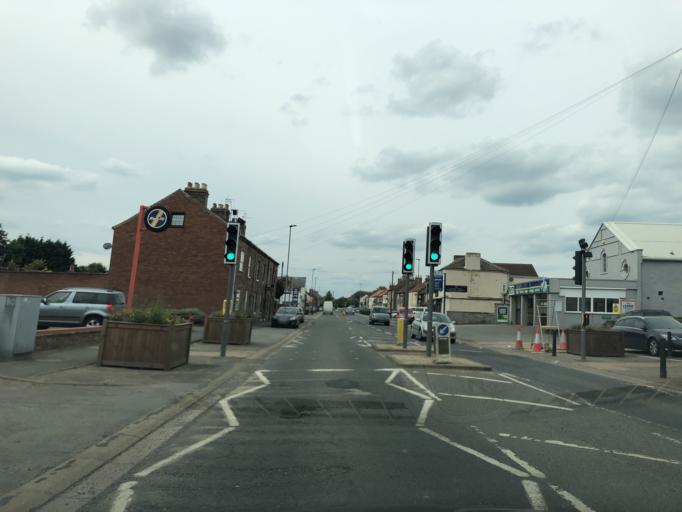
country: GB
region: England
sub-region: North Yorkshire
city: Thirsk
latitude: 54.2344
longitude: -1.3379
